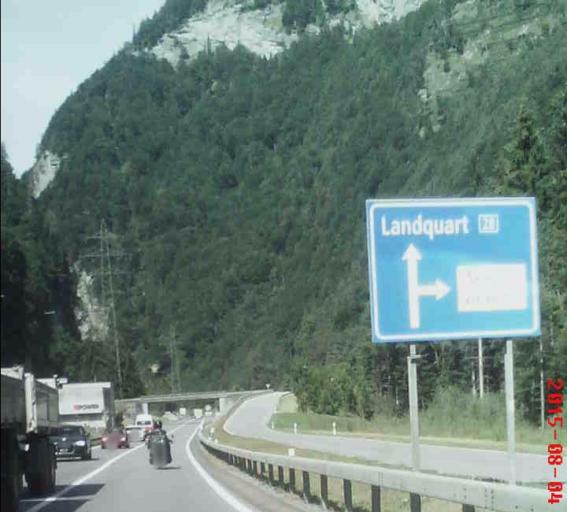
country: CH
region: Grisons
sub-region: Praettigau/Davos District
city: Grusch
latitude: 46.9747
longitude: 9.6356
